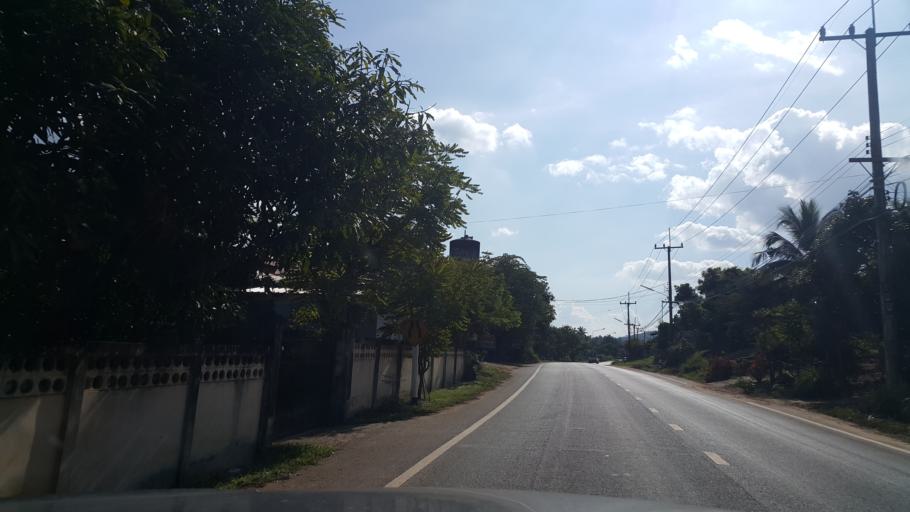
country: TH
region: Lamphun
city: Mae Tha
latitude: 18.5555
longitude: 99.2511
